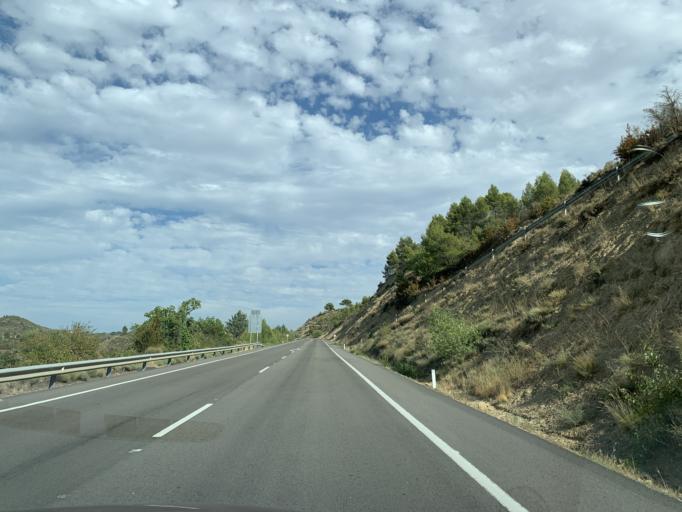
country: ES
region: Aragon
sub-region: Provincia de Zaragoza
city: Santa Eulalia de Gallego
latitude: 42.2925
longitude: -0.7236
